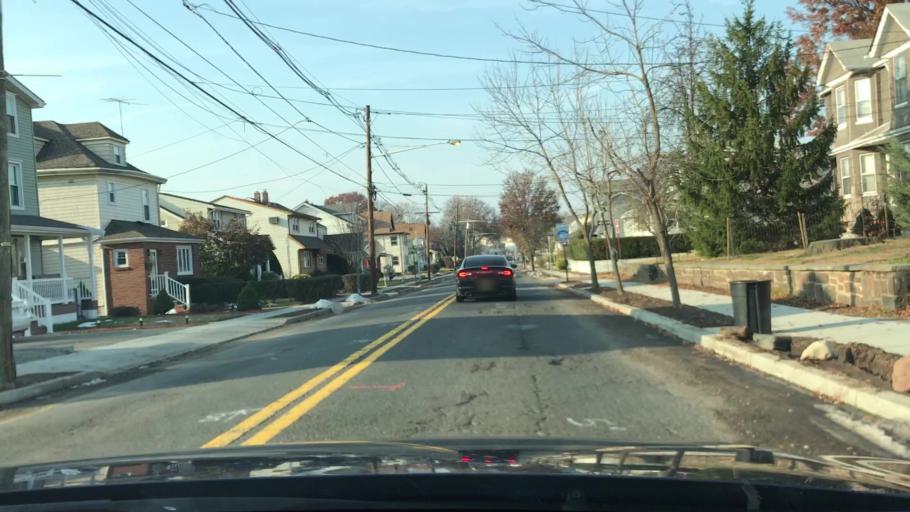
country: US
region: New Jersey
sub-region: Bergen County
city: Wallington
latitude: 40.8466
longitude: -74.1146
